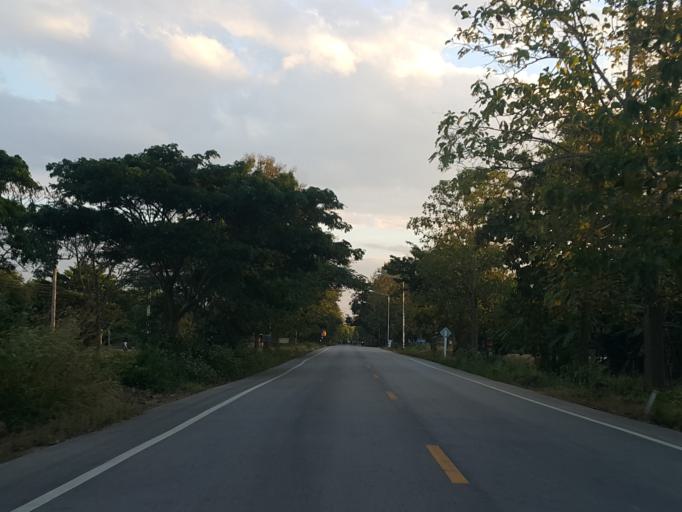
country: TH
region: Lampang
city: Mae Mo
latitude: 18.4541
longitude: 99.6345
